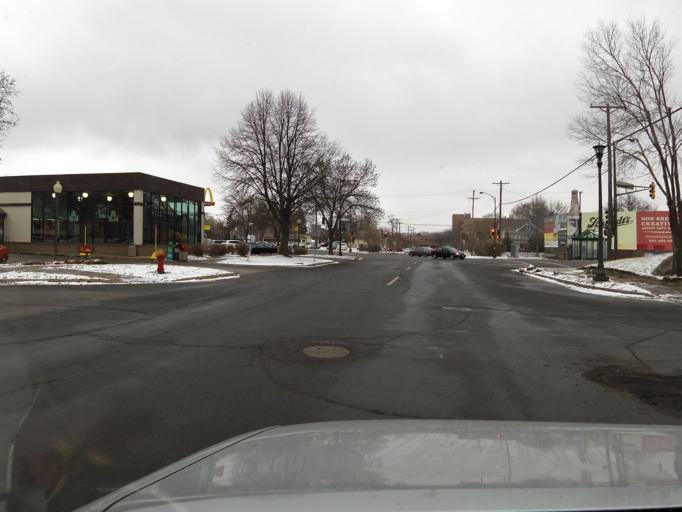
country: US
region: Minnesota
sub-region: Dakota County
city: West Saint Paul
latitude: 44.9306
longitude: -93.1233
